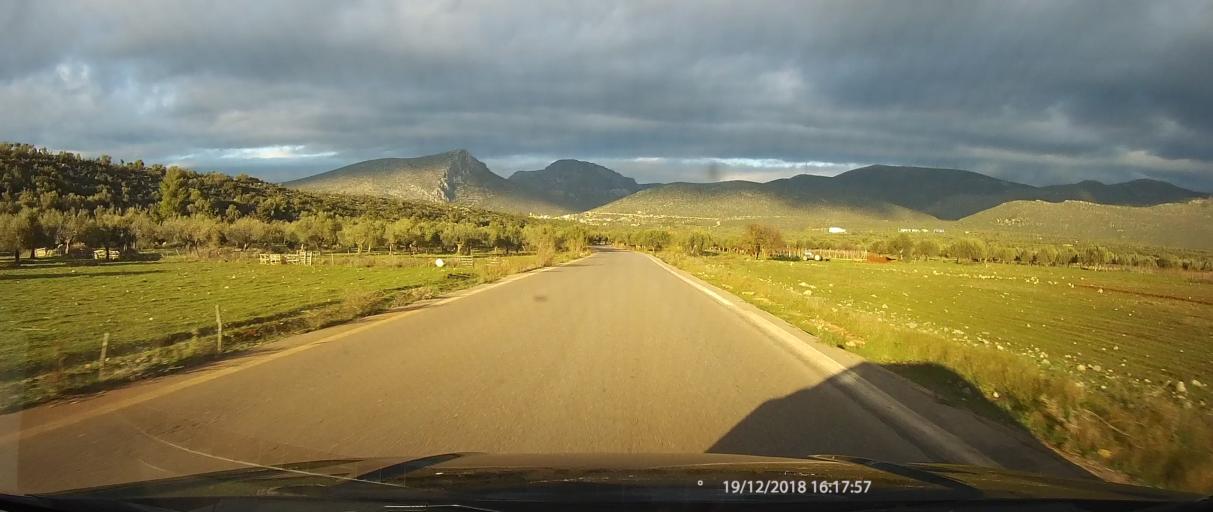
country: GR
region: Peloponnese
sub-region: Nomos Lakonias
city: Kato Glikovrisi
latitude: 36.9175
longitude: 22.8124
